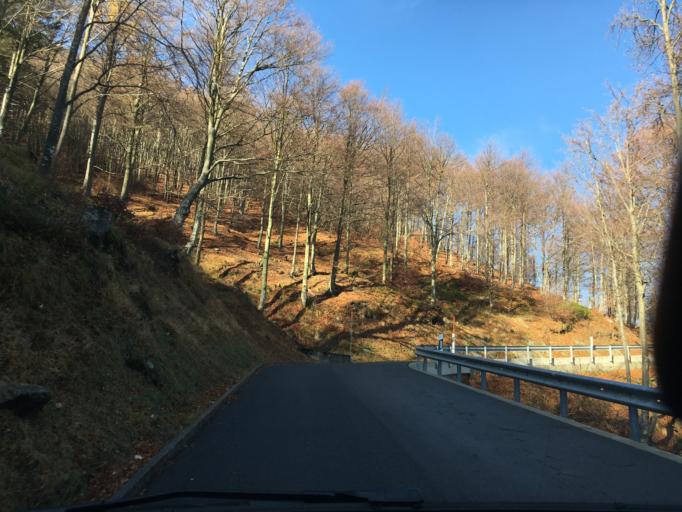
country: CH
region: Ticino
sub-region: Locarno District
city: Magadino
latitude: 46.1129
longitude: 8.8470
